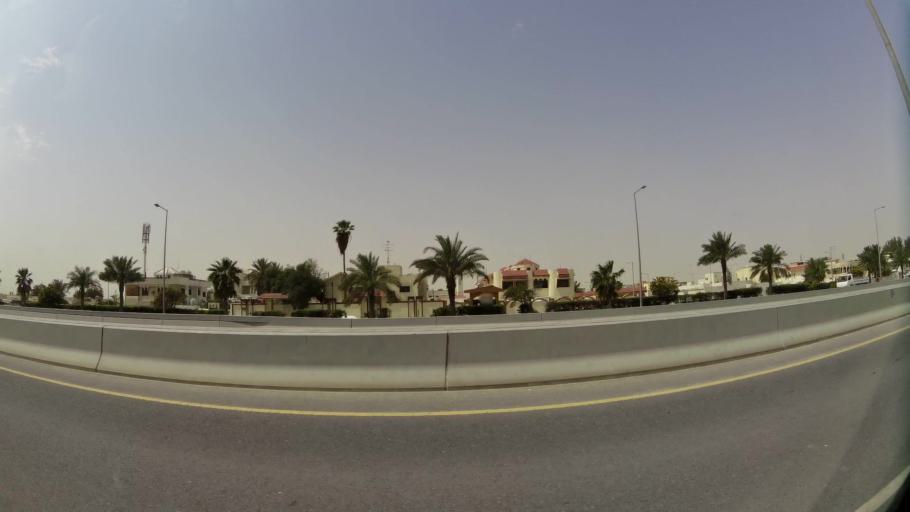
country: QA
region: Baladiyat ar Rayyan
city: Ar Rayyan
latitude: 25.2296
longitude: 51.4313
